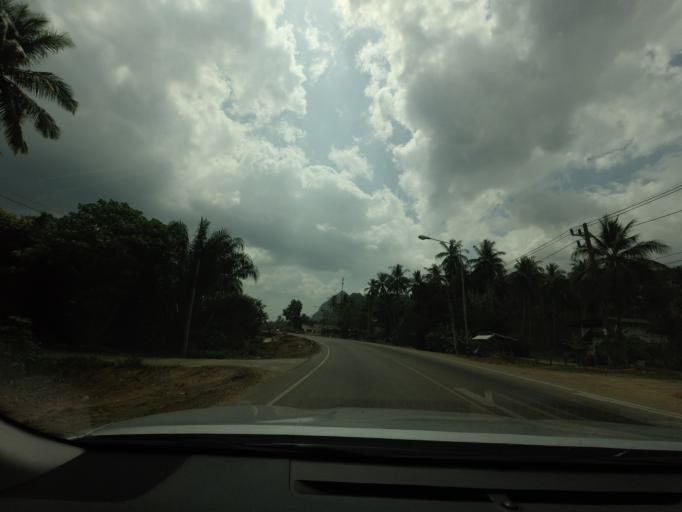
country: TH
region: Phangnga
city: Ban Ao Nang
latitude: 8.1034
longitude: 98.8014
